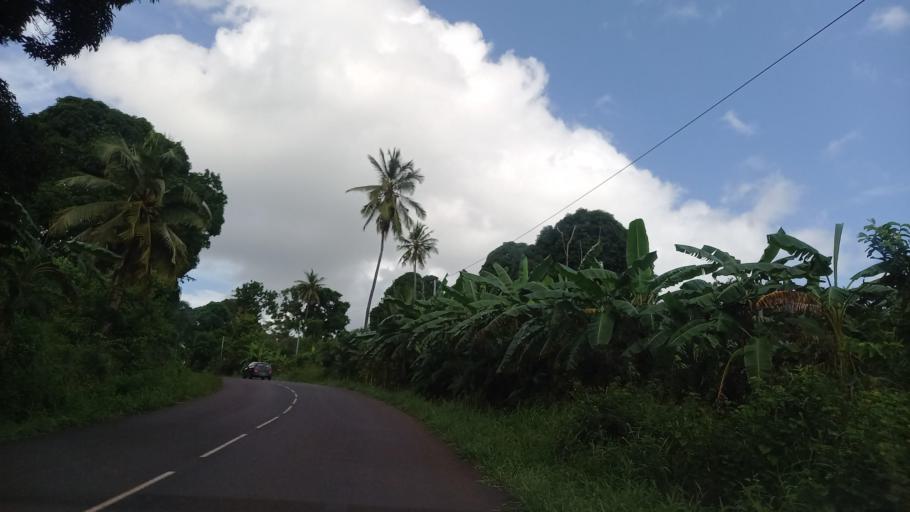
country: YT
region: Boueni
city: Boueni
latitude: -12.9186
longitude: 45.1015
